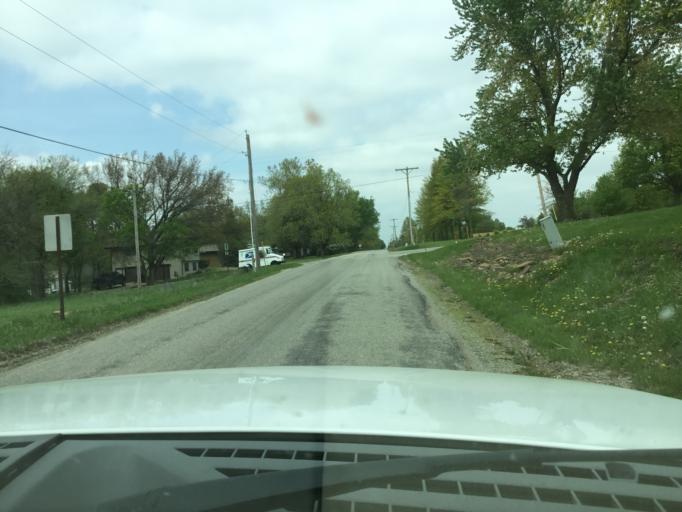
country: US
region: Kansas
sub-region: Shawnee County
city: Topeka
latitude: 39.0001
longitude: -95.5863
